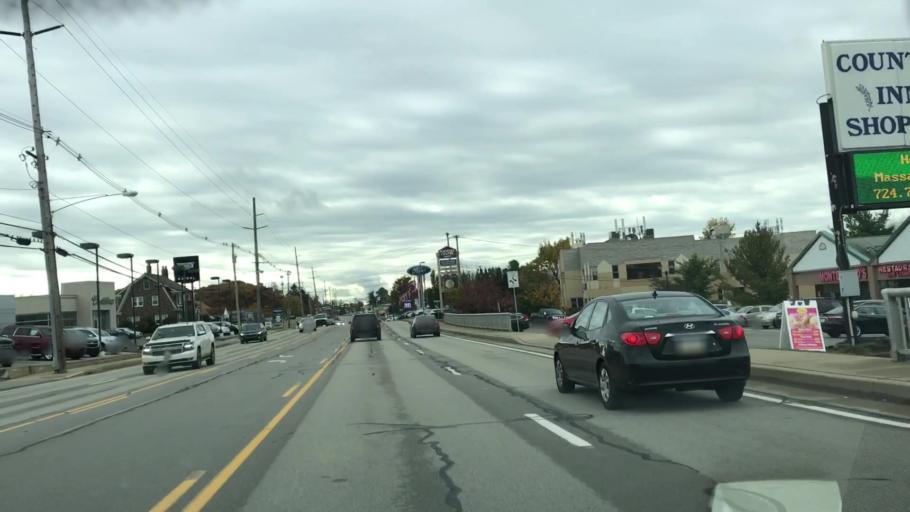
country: US
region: Pennsylvania
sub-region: Allegheny County
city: Bradford Woods
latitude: 40.6070
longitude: -80.0520
